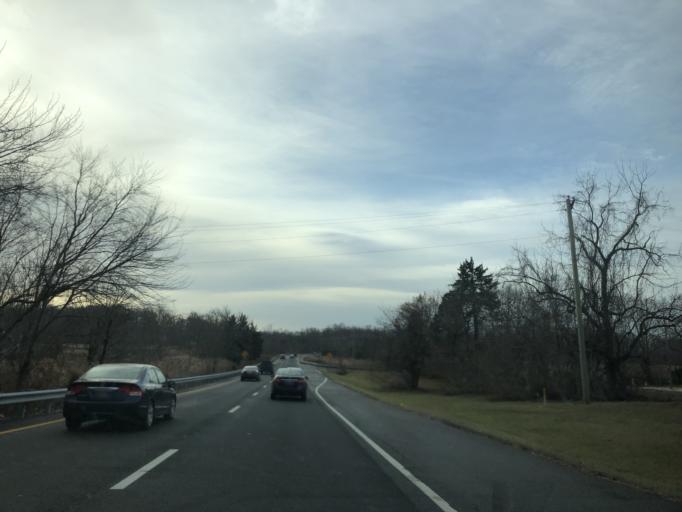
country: US
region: Delaware
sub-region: New Castle County
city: Middletown
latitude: 39.4746
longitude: -75.6515
